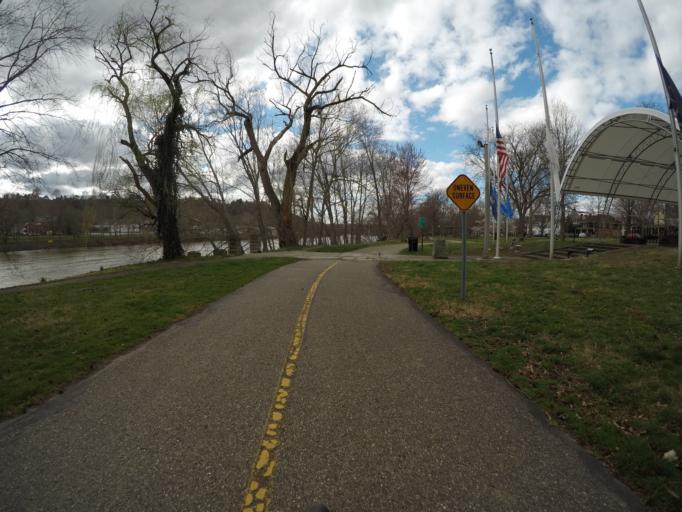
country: US
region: Ohio
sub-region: Washington County
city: Marietta
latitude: 39.4154
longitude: -81.4578
